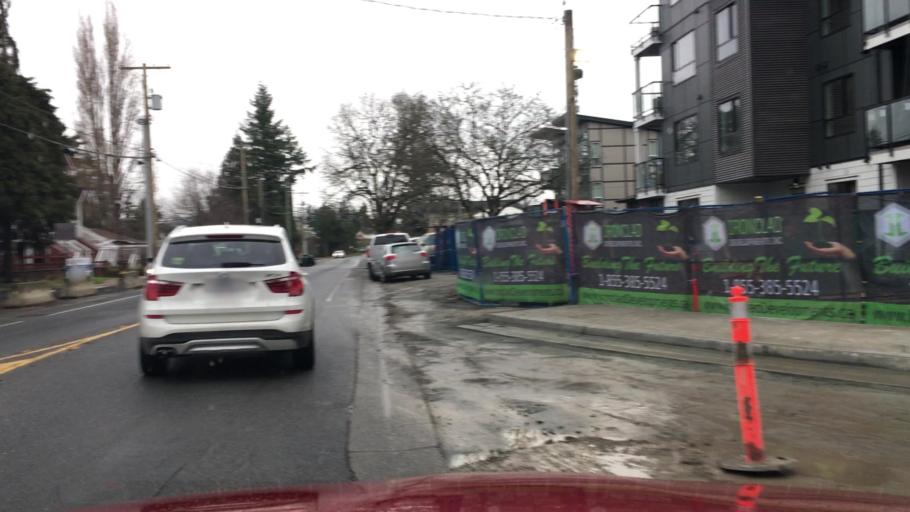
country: CA
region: British Columbia
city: Langford
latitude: 48.4530
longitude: -123.4984
